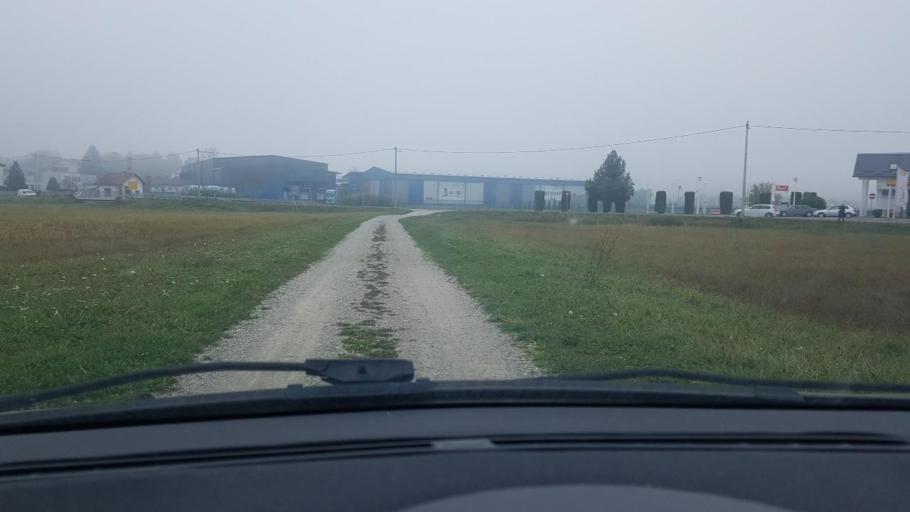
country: HR
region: Krapinsko-Zagorska
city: Marija Bistrica
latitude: 46.0540
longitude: 16.1725
